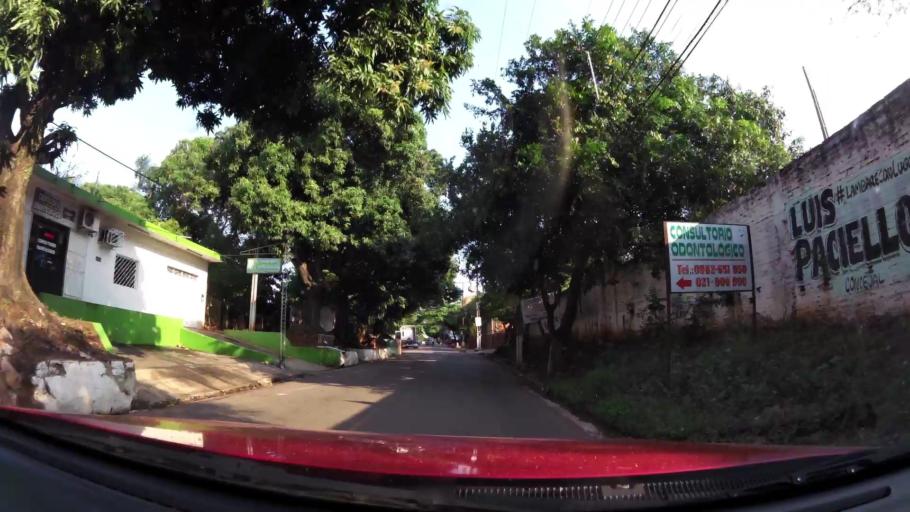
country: PY
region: Central
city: Lambare
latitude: -25.3412
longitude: -57.5931
